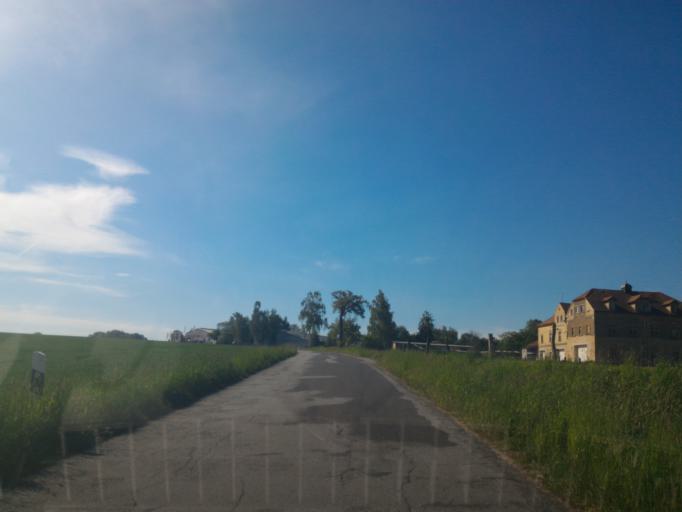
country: DE
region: Saxony
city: Grossschweidnitz
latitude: 51.0584
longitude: 14.6369
